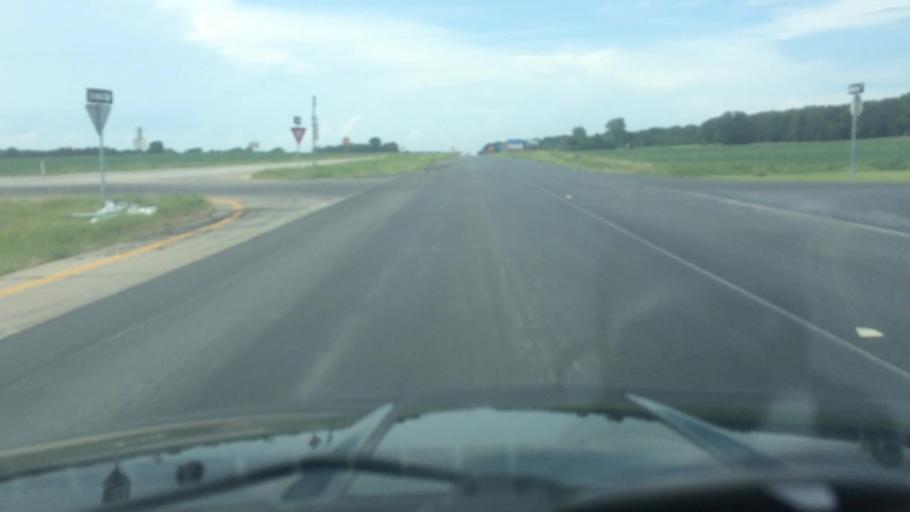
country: US
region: Missouri
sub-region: Saint Clair County
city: Osceola
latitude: 37.9895
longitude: -93.6517
